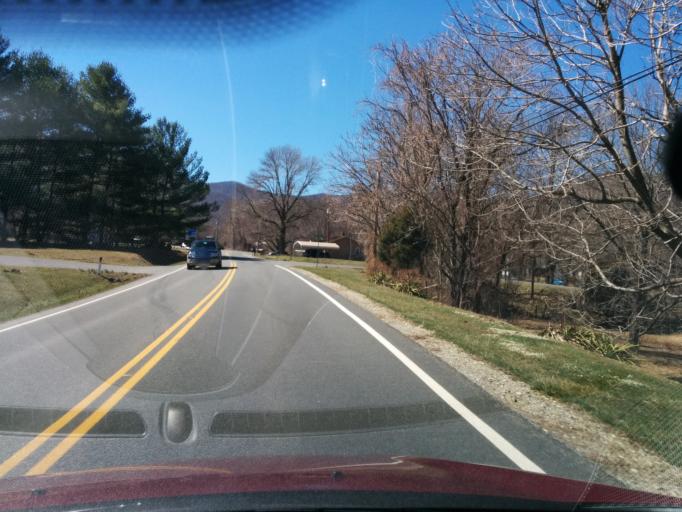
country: US
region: Virginia
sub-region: Nelson County
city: Nellysford
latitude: 37.8748
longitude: -78.9343
